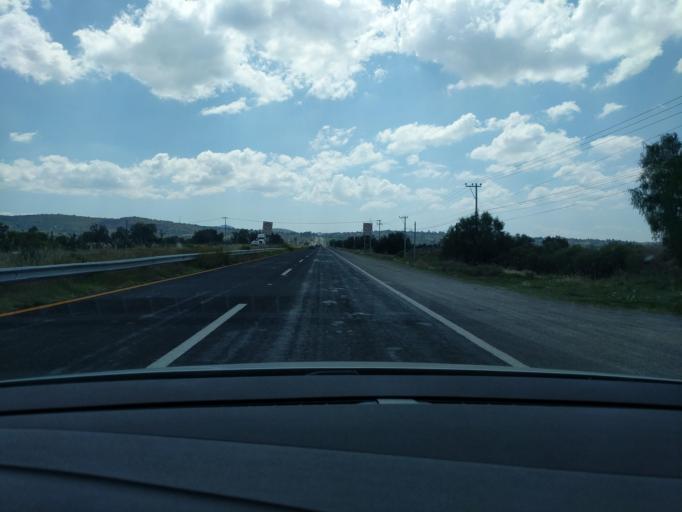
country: MX
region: Hidalgo
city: Zempoala
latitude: 19.9413
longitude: -98.6878
